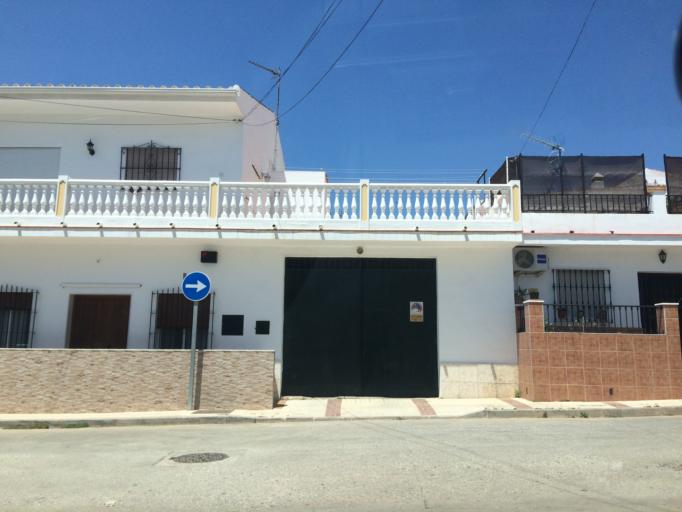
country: ES
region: Andalusia
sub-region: Provincia de Malaga
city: Malaga
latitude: 36.7342
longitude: -4.4808
